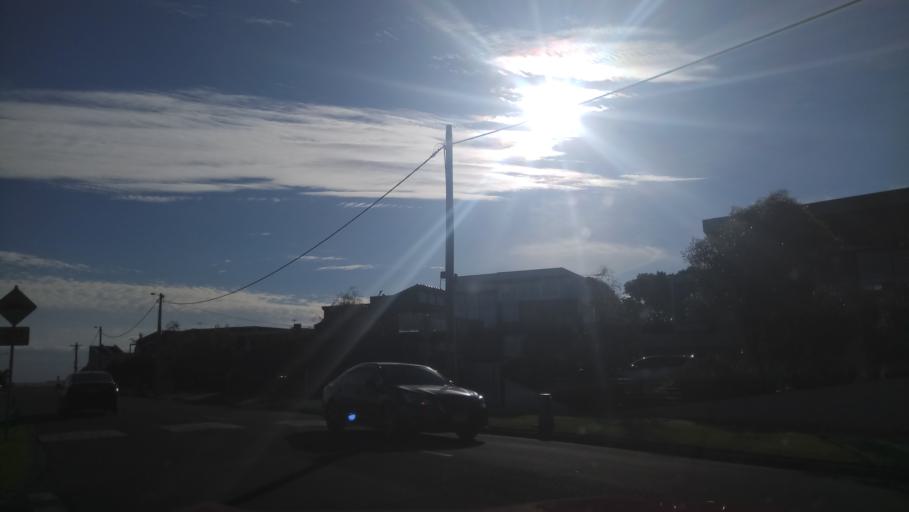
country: AU
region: Victoria
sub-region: Hobsons Bay
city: Williamstown
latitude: -37.8702
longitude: 144.9037
